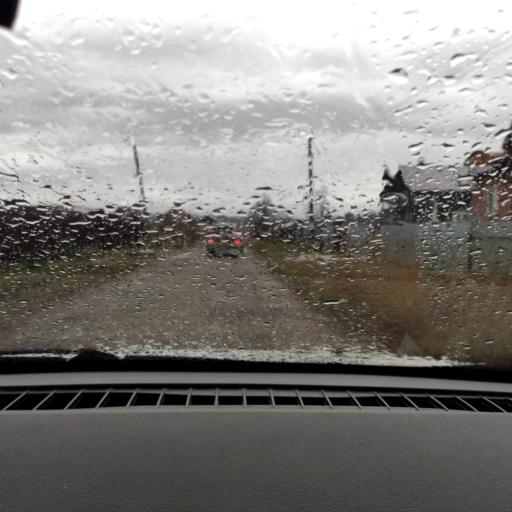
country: RU
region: Perm
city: Kultayevo
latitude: 57.8968
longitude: 55.9569
